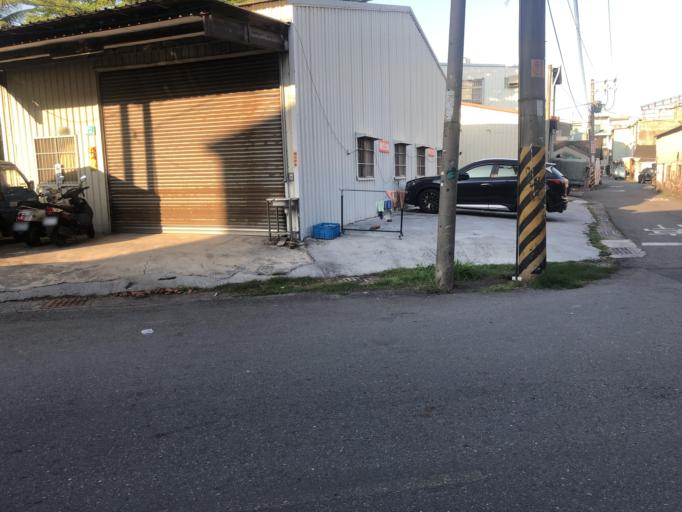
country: TW
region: Taiwan
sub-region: Tainan
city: Tainan
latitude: 23.0397
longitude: 120.1847
